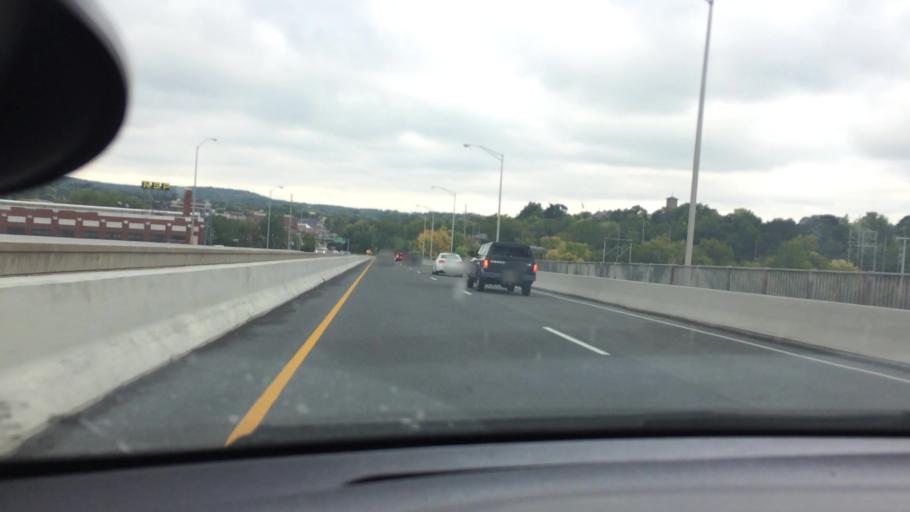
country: US
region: Wisconsin
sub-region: Chippewa County
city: Chippewa Falls
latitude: 44.9303
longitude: -91.3865
